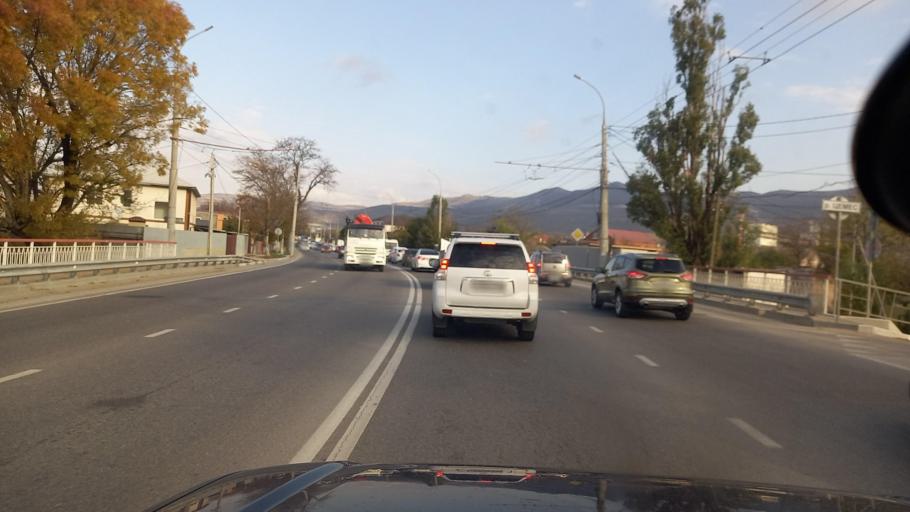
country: RU
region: Krasnodarskiy
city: Gayduk
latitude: 44.7510
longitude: 37.7275
